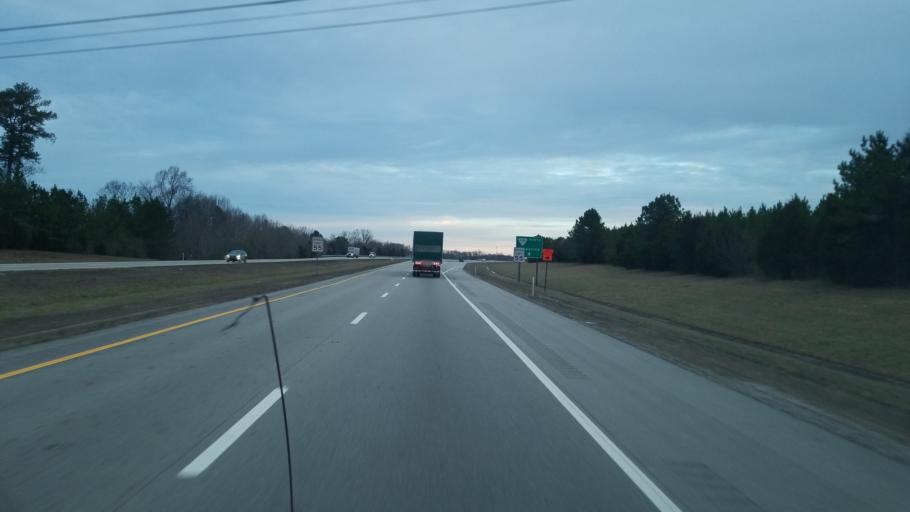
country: US
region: Tennessee
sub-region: Putnam County
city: Cookeville
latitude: 36.0955
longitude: -85.5051
